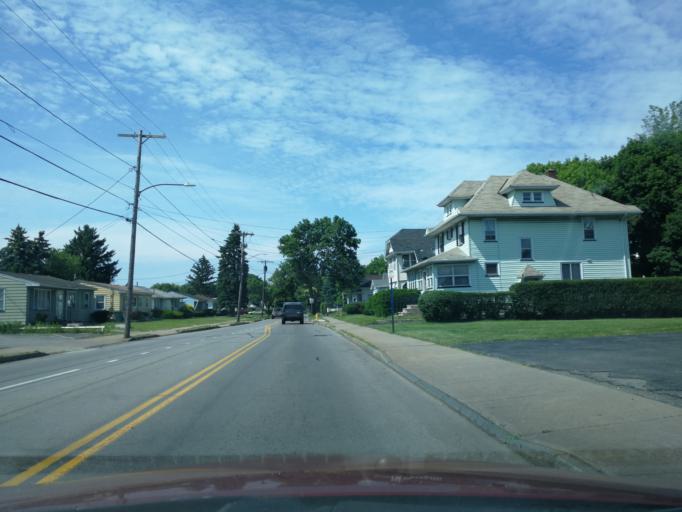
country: US
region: New York
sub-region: Monroe County
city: Irondequoit
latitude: 43.1874
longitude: -77.5919
